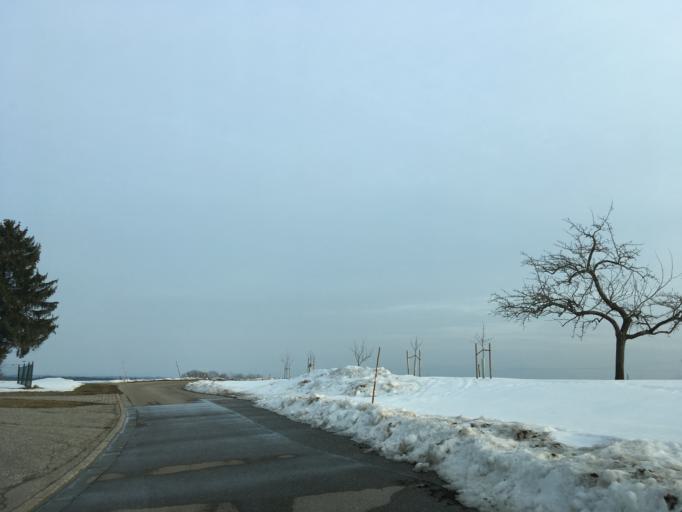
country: DE
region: Bavaria
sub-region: Upper Bavaria
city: Bad Endorf
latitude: 47.9178
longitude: 12.3309
